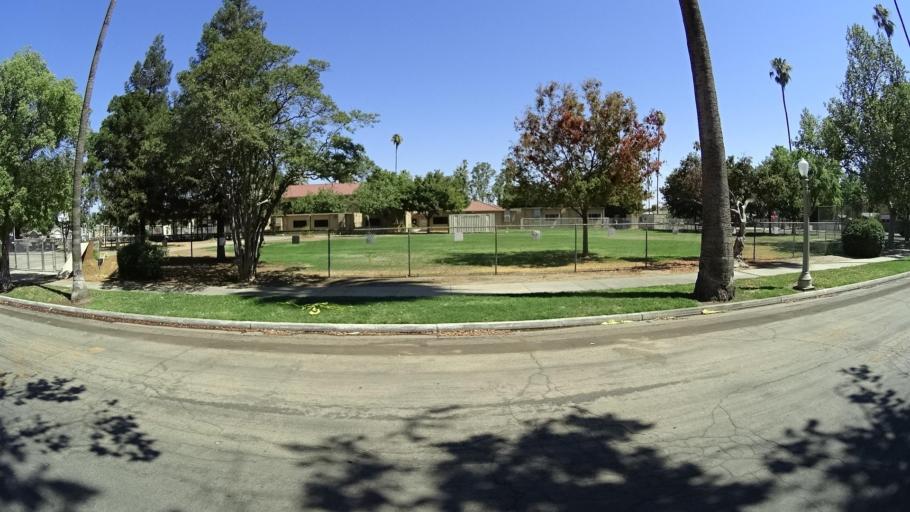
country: US
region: California
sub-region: Fresno County
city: Fresno
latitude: 36.7406
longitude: -119.7617
